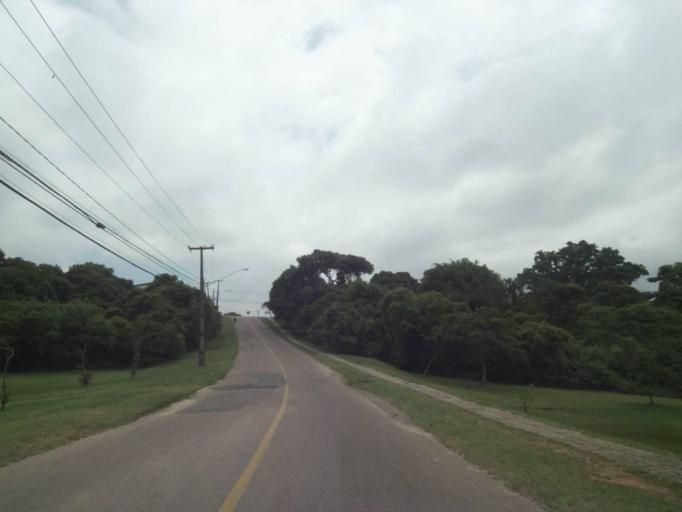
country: BR
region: Parana
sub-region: Curitiba
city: Curitiba
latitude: -25.4915
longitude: -49.3493
